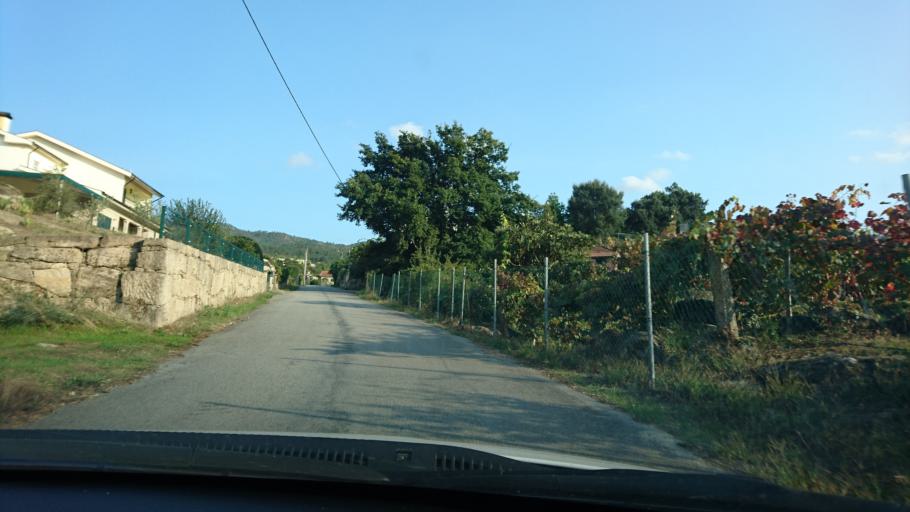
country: PT
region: Vila Real
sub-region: Mondim de Basto
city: Mondim de Basto
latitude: 41.4445
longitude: -7.9289
